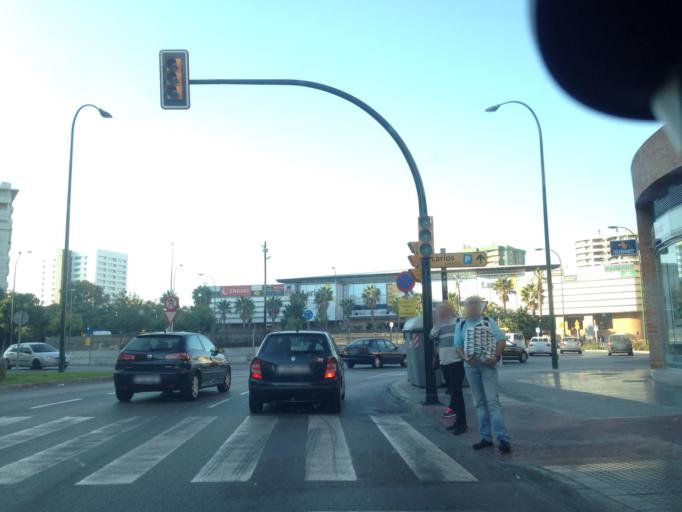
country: ES
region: Andalusia
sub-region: Provincia de Malaga
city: Malaga
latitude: 36.7136
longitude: -4.4320
